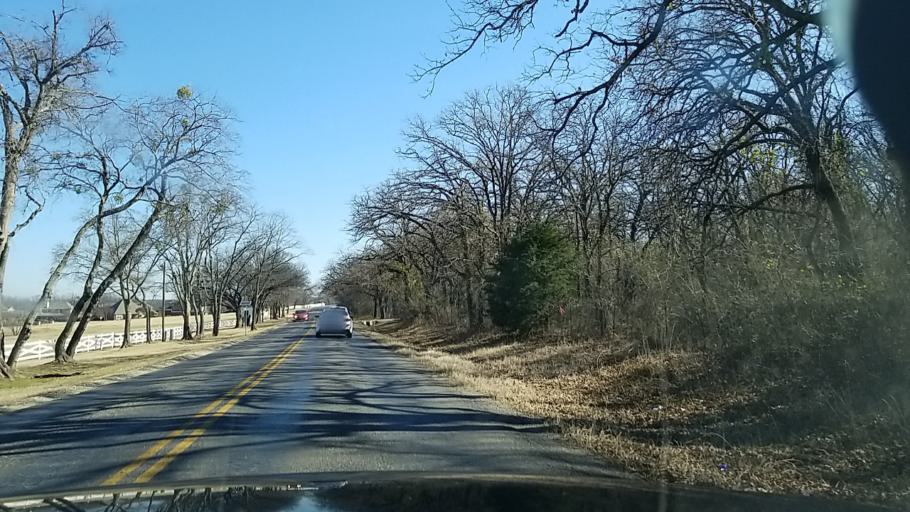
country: US
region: Texas
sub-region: Denton County
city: Argyle
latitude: 33.1288
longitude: -97.1917
